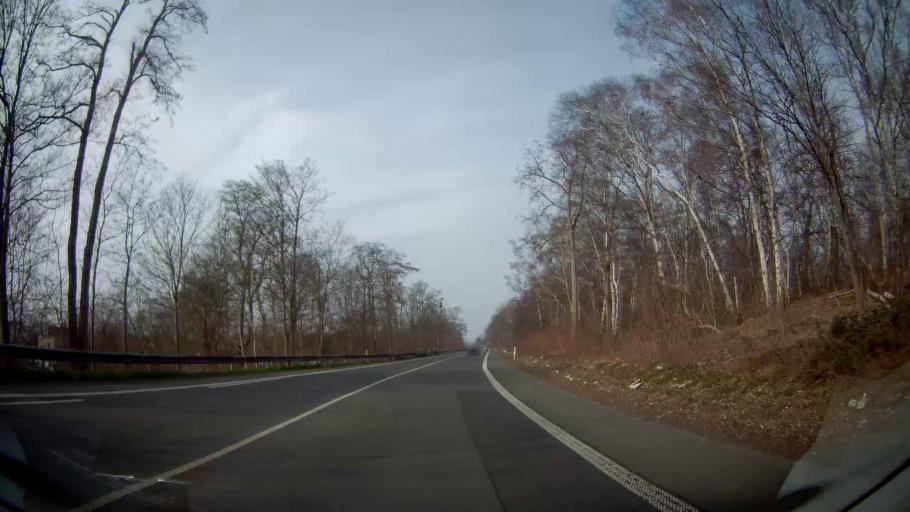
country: DE
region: North Rhine-Westphalia
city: Meiderich
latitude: 51.4581
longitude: 6.7071
